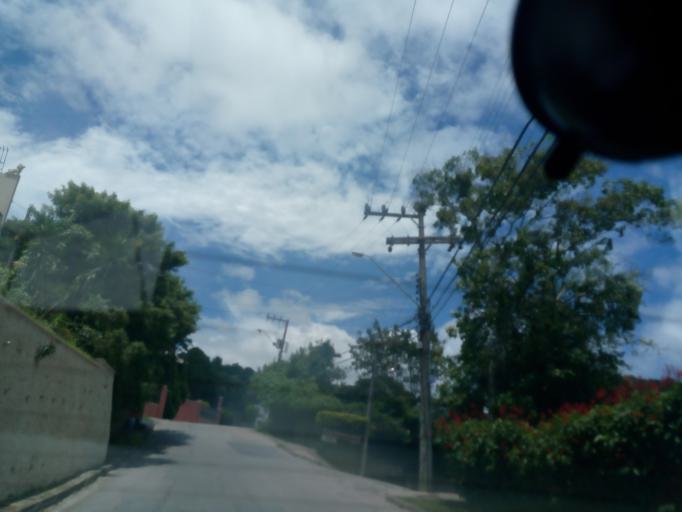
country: BR
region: Santa Catarina
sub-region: Florianopolis
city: Itacorubi
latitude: -27.3923
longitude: -48.4214
